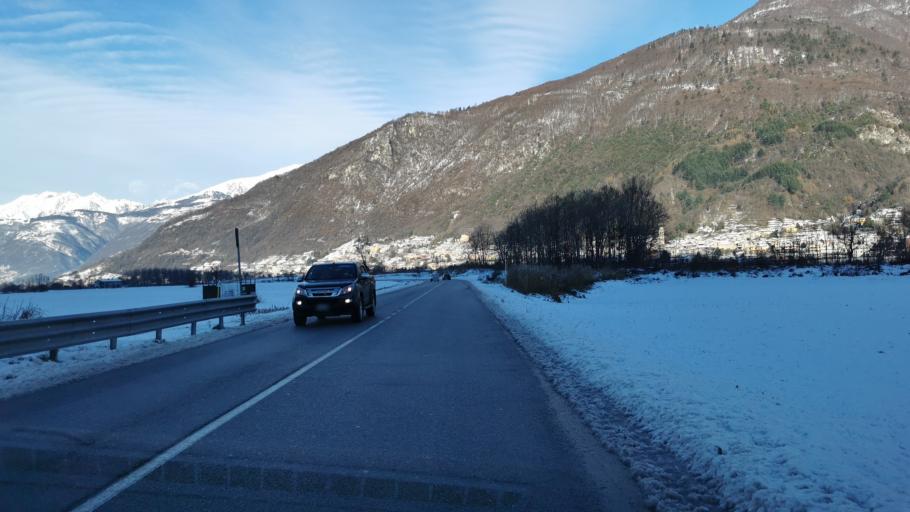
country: IT
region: Lombardy
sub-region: Provincia di Sondrio
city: Delebio
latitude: 46.1453
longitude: 9.4666
